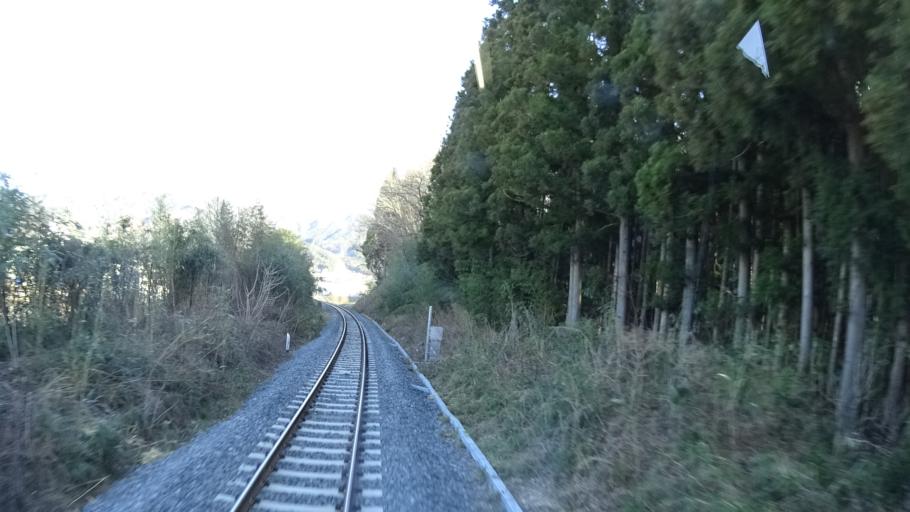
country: JP
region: Iwate
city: Miyako
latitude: 39.5924
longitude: 141.9431
